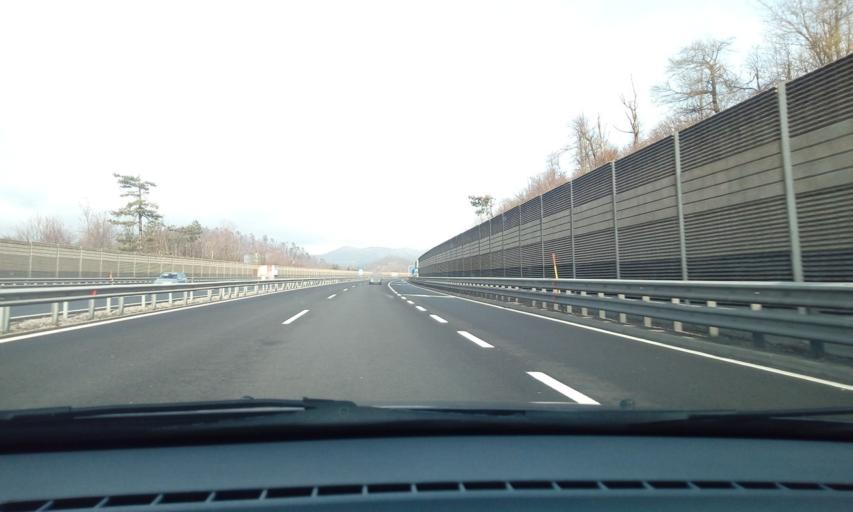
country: SI
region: Postojna
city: Postojna
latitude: 45.7777
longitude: 14.2220
